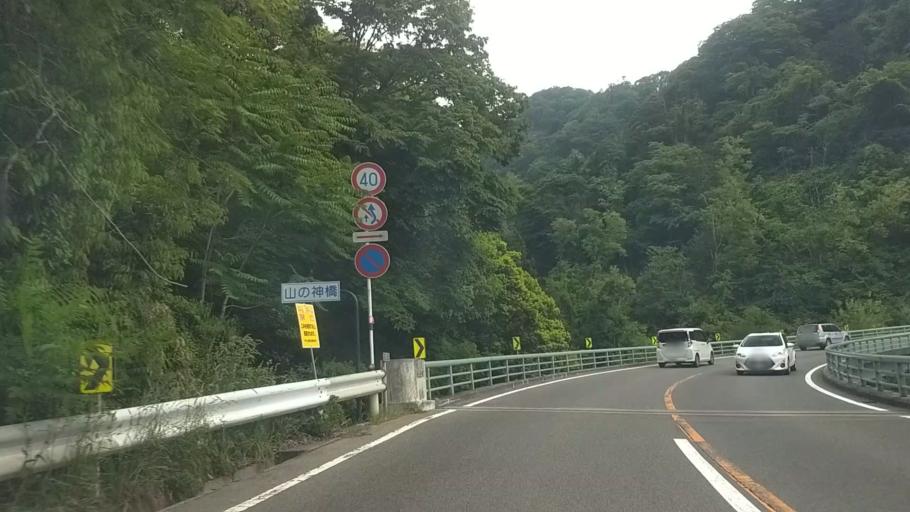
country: JP
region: Yamanashi
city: Isawa
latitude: 35.5621
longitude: 138.5938
